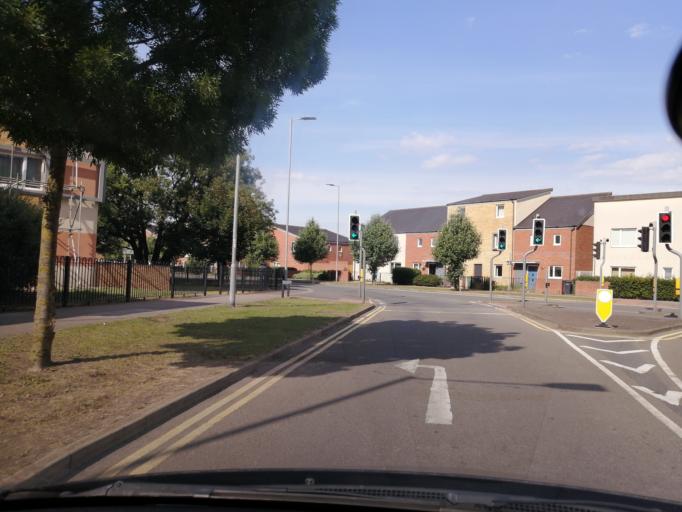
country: GB
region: England
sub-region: Peterborough
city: Peterborough
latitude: 52.5517
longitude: -0.2496
